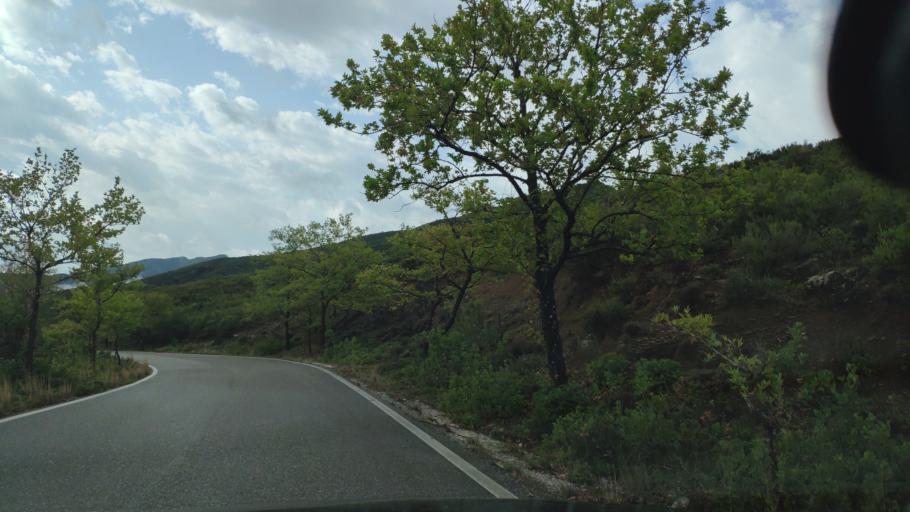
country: GR
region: West Greece
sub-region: Nomos Aitolias kai Akarnanias
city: Sardinia
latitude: 38.8451
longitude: 21.3168
